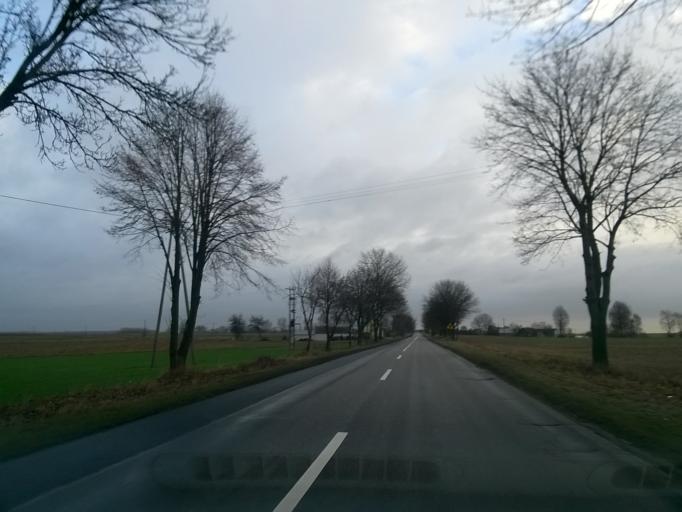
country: PL
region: Greater Poland Voivodeship
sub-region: Powiat wagrowiecki
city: Golancz
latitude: 52.8799
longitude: 17.3214
